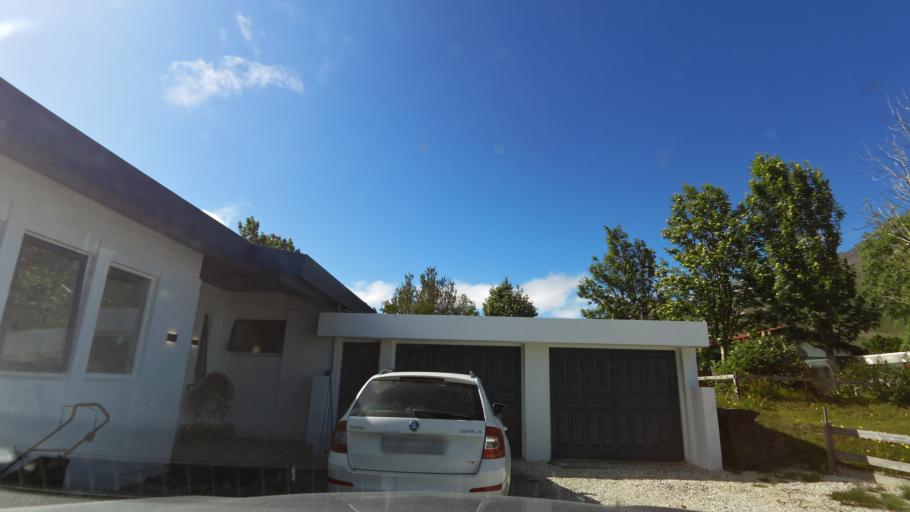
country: IS
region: Westfjords
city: Isafjoerdur
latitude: 66.0553
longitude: -23.1755
